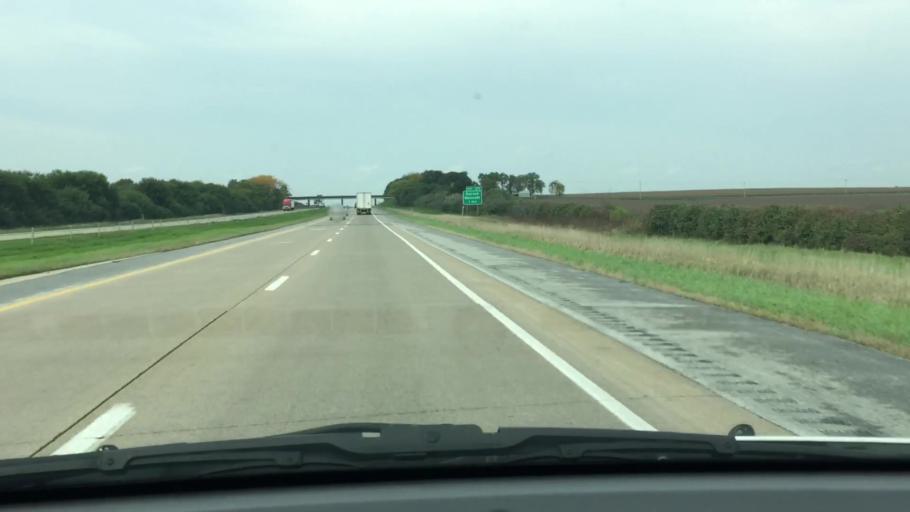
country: US
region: Iowa
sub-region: Cedar County
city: Durant
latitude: 41.6331
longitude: -90.8931
